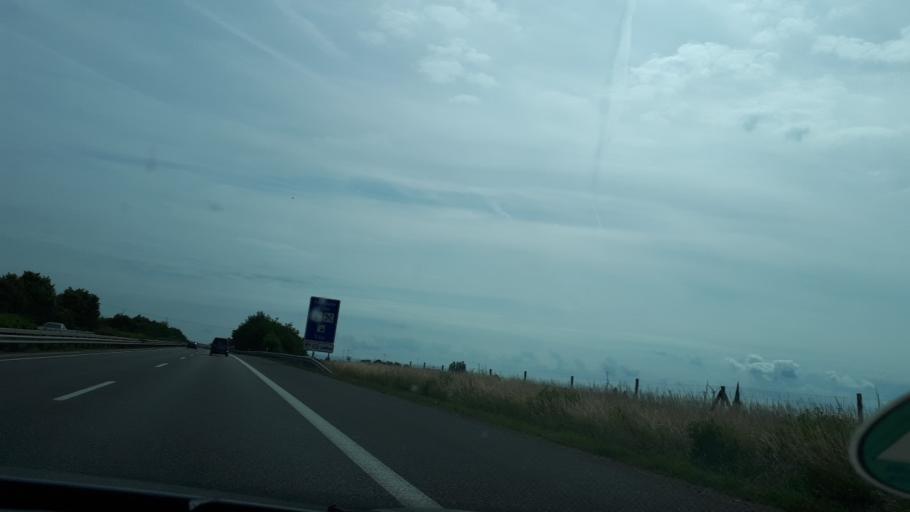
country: DE
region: Rheinland-Pfalz
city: Hambuch
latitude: 50.2273
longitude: 7.1752
